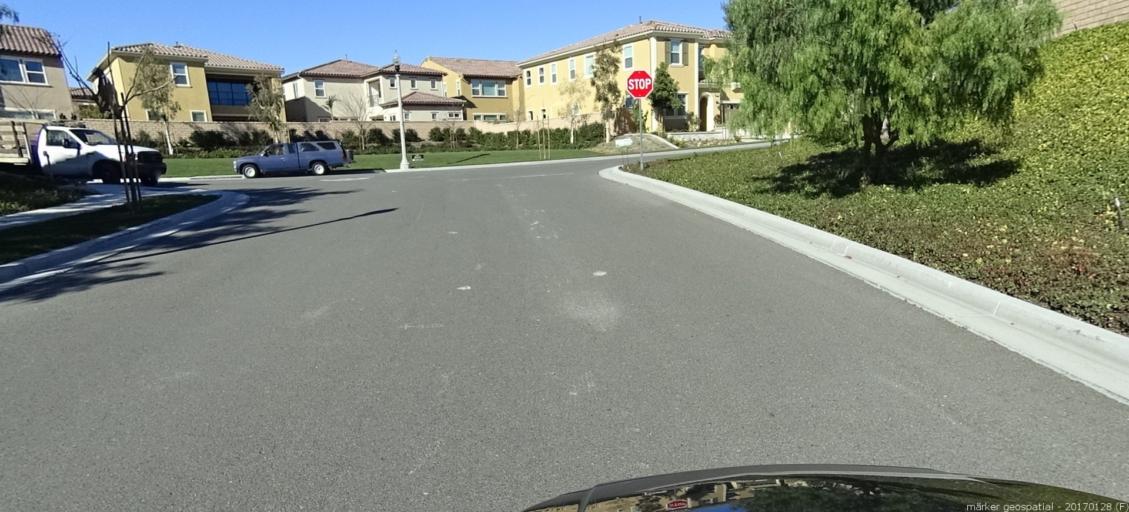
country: US
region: California
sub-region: Orange County
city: Lake Forest
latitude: 33.6689
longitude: -117.6881
